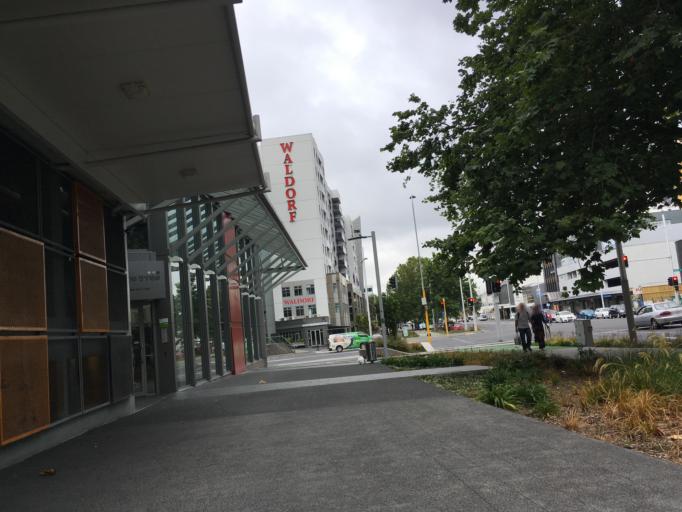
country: NZ
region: Auckland
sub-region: Auckland
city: Auckland
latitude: -36.8460
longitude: 174.7727
